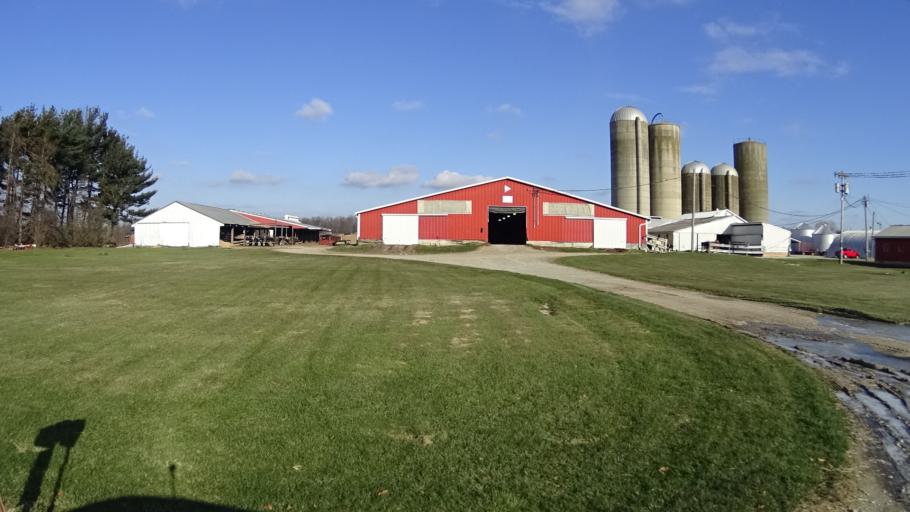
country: US
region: Ohio
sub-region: Lorain County
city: Wellington
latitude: 41.2235
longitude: -82.2384
